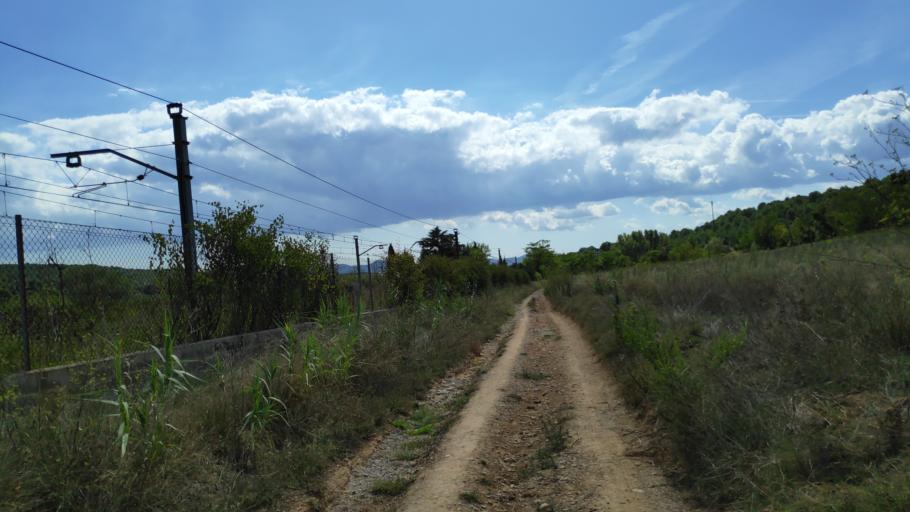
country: ES
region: Catalonia
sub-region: Provincia de Barcelona
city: Rubi
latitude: 41.5213
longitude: 2.0334
